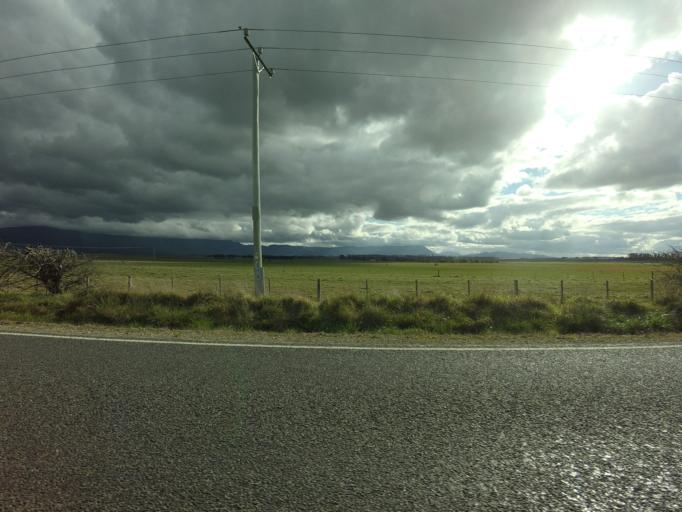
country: AU
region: Tasmania
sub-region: Northern Midlands
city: Longford
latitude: -41.7469
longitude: 147.0823
